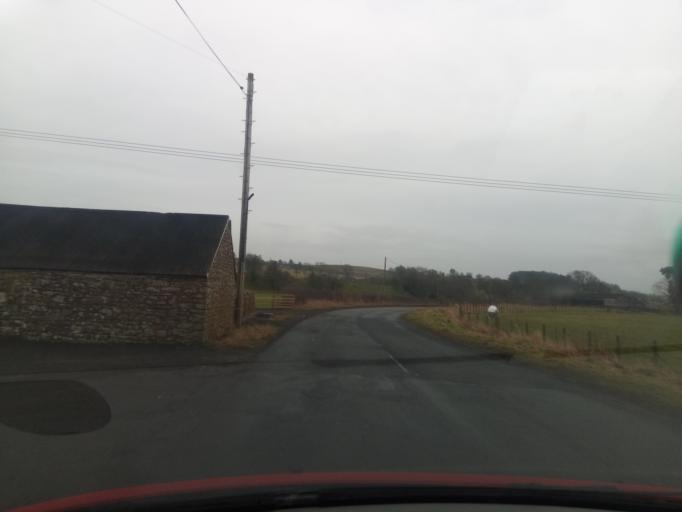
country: GB
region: England
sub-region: Northumberland
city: Rochester
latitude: 55.1644
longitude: -2.3402
